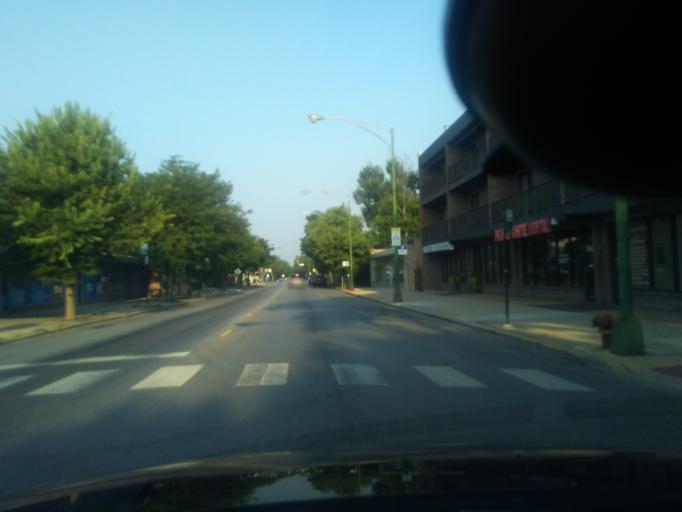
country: US
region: Illinois
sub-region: Cook County
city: Evanston
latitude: 42.0122
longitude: -87.6974
